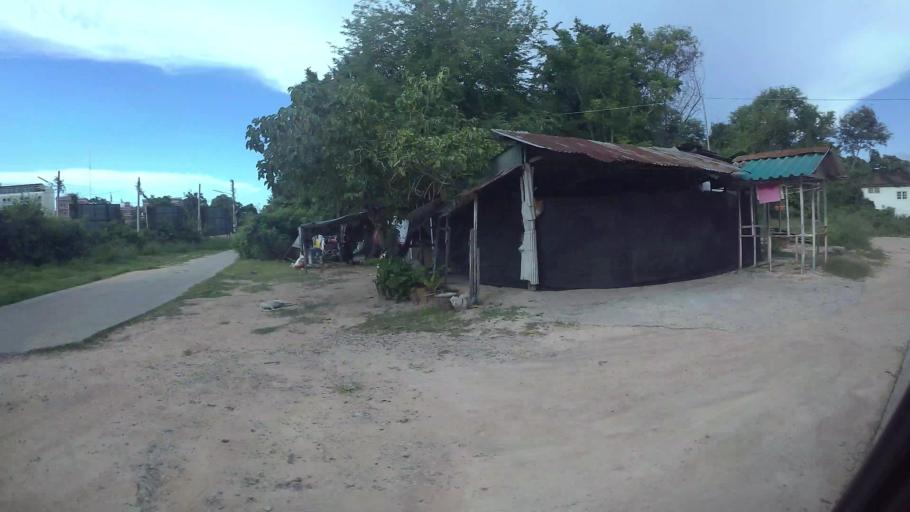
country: TH
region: Chon Buri
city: Phatthaya
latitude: 12.9115
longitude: 100.8716
